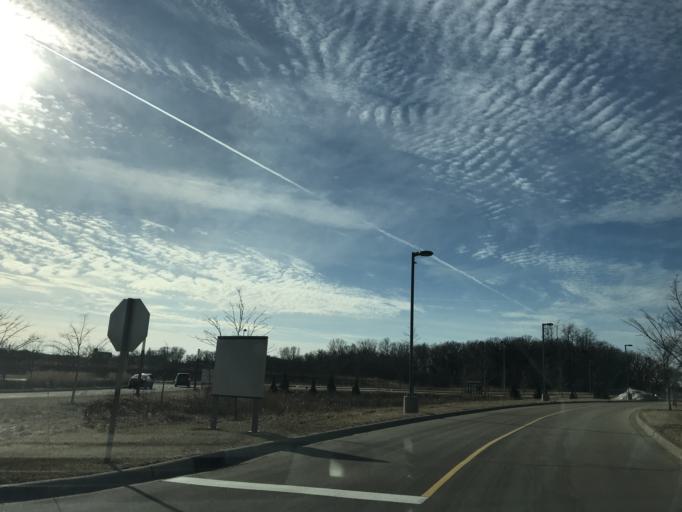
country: US
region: Wisconsin
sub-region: Dane County
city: Windsor
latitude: 43.1543
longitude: -89.3002
